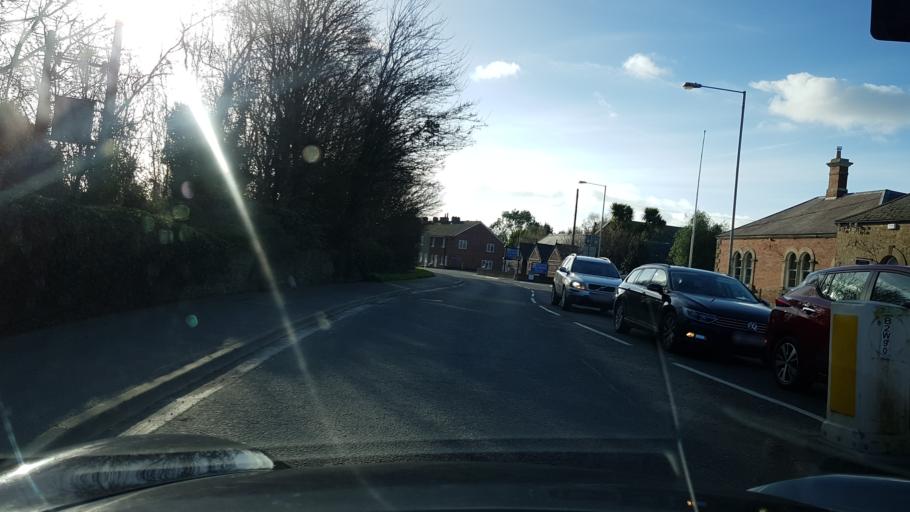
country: GB
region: England
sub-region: Dorset
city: Bridport
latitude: 50.7265
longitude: -2.7580
